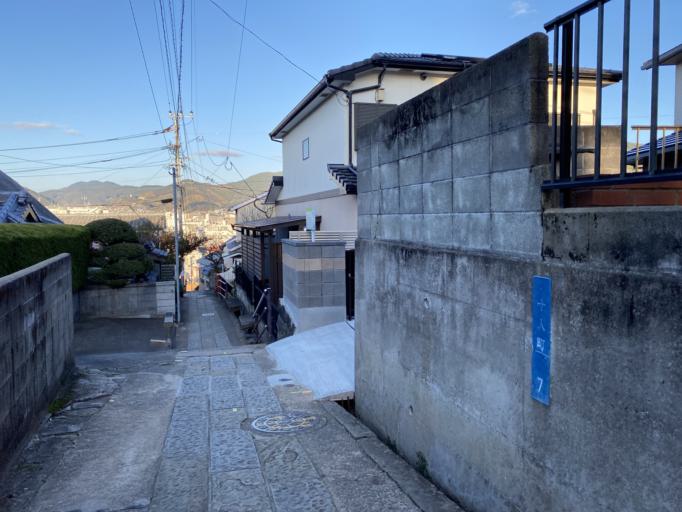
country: JP
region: Nagasaki
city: Nagasaki-shi
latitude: 32.7387
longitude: 129.8744
